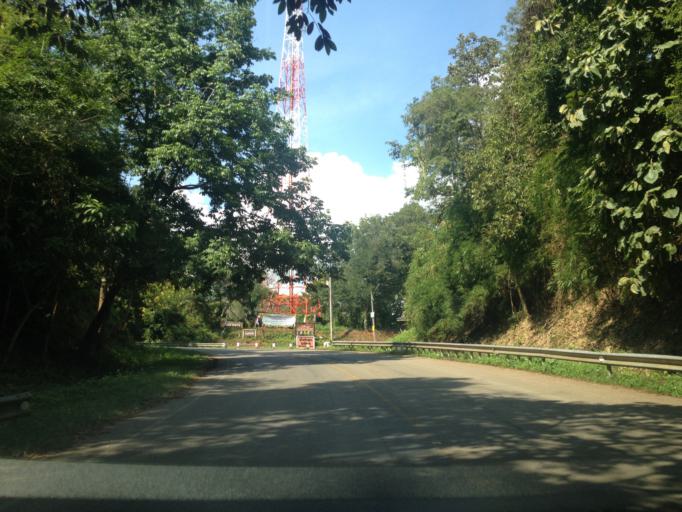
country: TH
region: Chiang Mai
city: Samoeng
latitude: 18.8064
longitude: 98.8290
